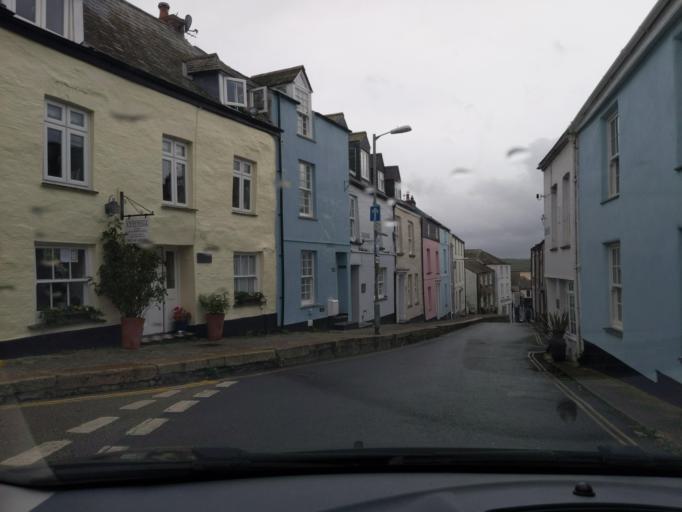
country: GB
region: England
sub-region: Cornwall
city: Padstow
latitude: 50.5417
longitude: -4.9410
